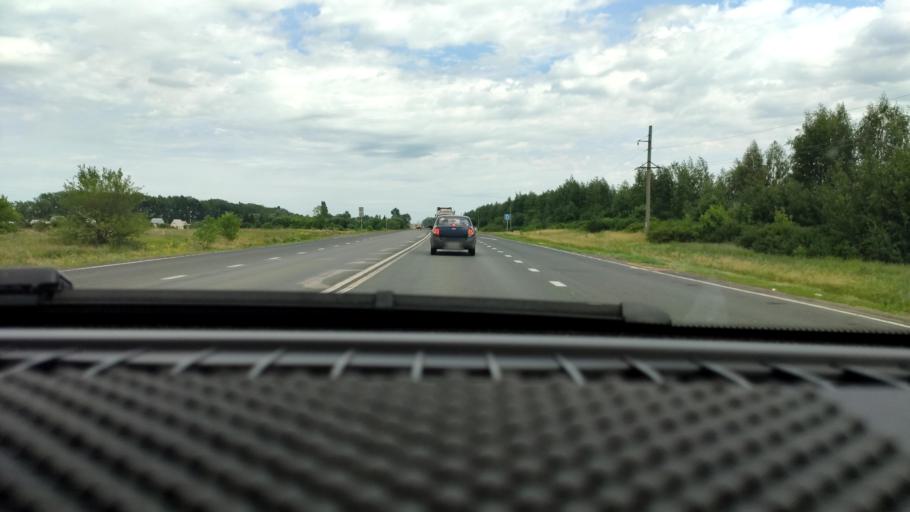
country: RU
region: Voronezj
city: Orlovo
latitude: 51.6799
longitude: 39.6271
